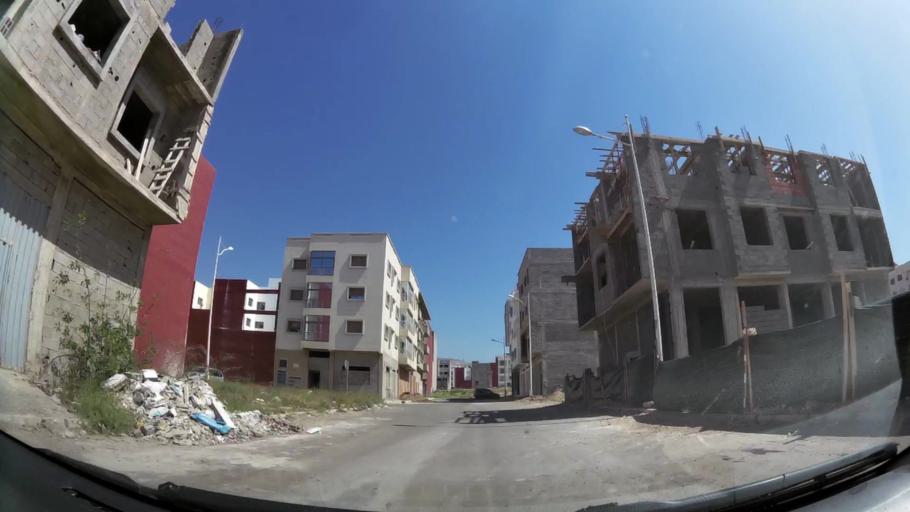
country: MA
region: Oued ed Dahab-Lagouira
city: Dakhla
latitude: 30.4415
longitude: -9.5608
